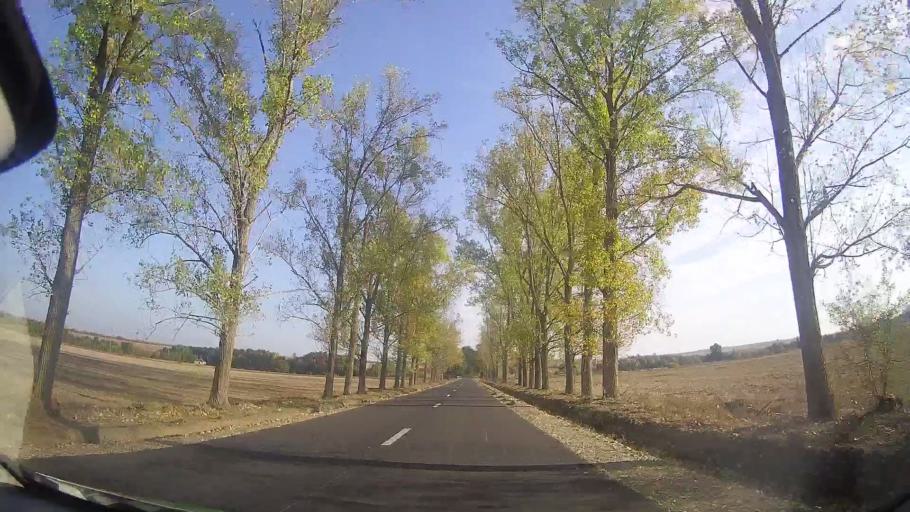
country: RO
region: Timis
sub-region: Comuna Masloc
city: Masloc
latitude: 45.9722
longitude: 21.4946
